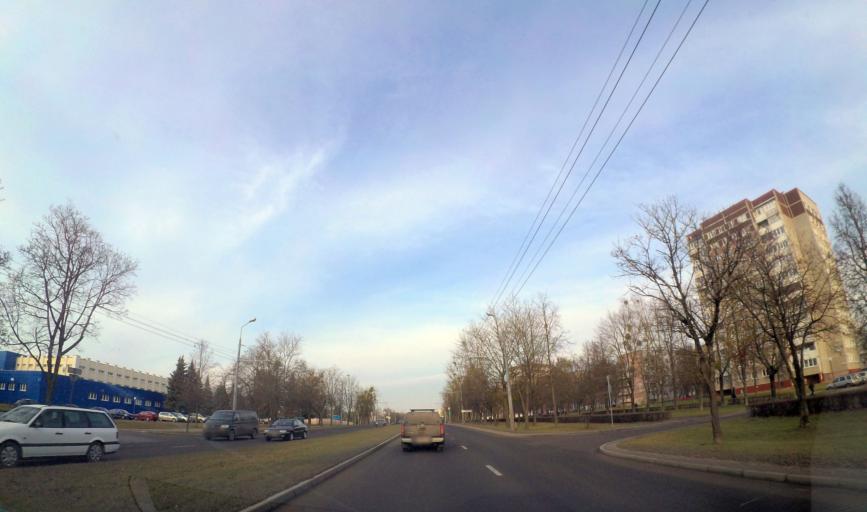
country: BY
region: Grodnenskaya
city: Hrodna
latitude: 53.6909
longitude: 23.8009
